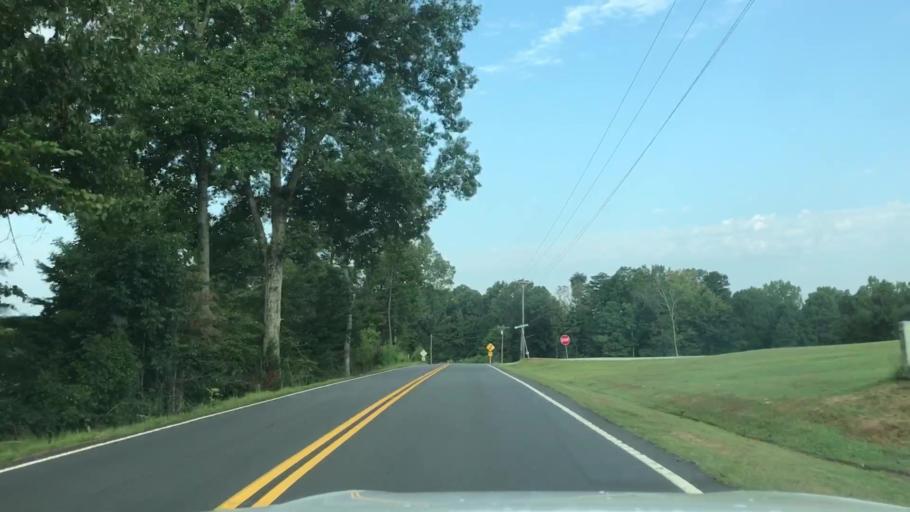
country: US
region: South Carolina
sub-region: Spartanburg County
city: Roebuck
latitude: 34.8214
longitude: -81.9362
